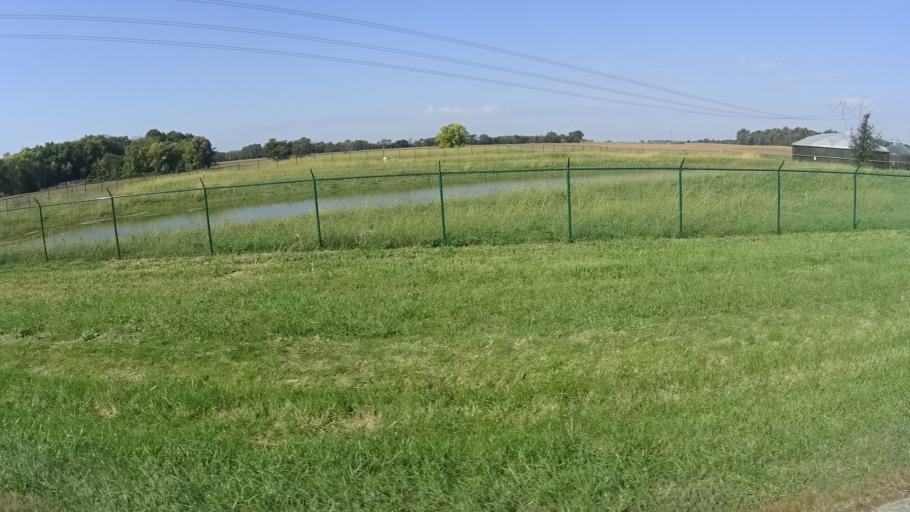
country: US
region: Indiana
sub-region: Madison County
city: Lapel
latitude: 40.0261
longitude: -85.8433
